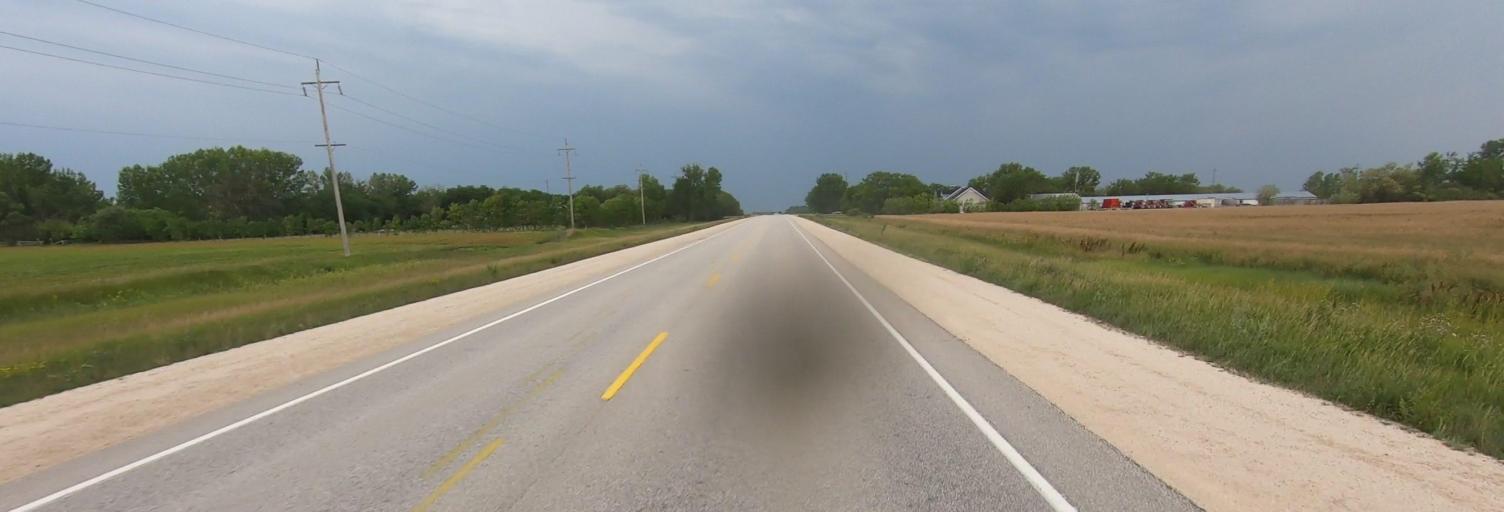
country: CA
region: Manitoba
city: Headingley
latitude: 49.7685
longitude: -97.3630
